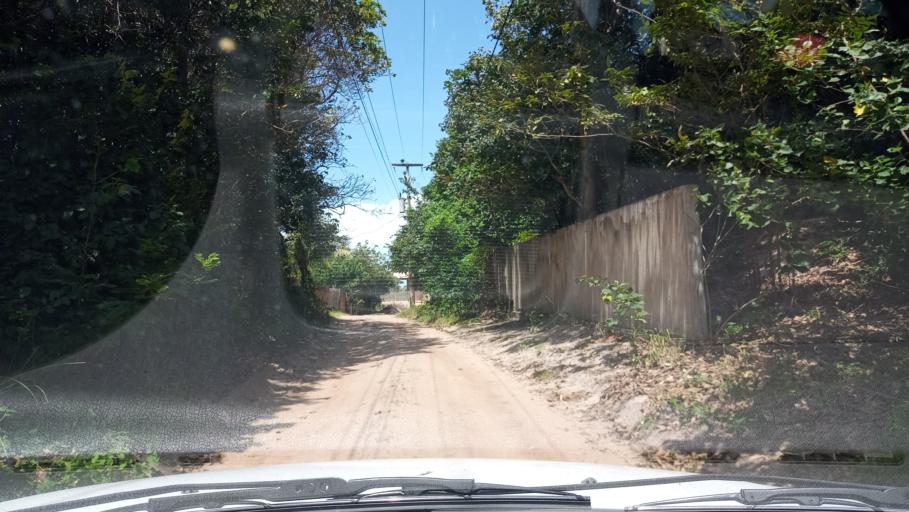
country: BR
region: Rio Grande do Norte
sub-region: Ares
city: Ares
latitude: -6.2433
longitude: -35.0435
